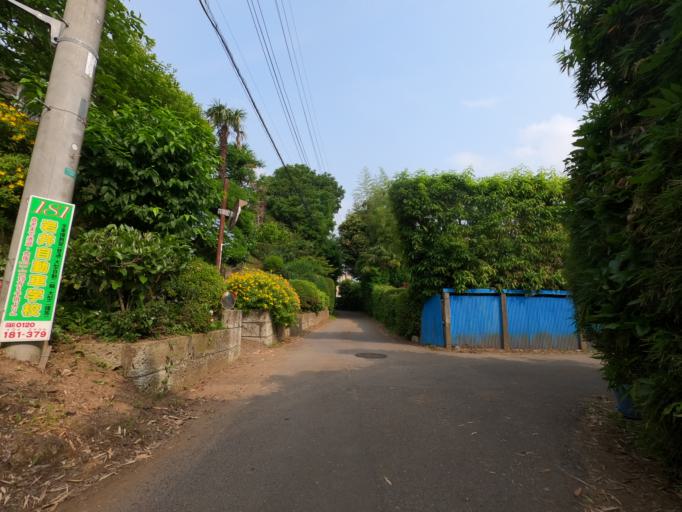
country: JP
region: Ibaraki
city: Moriya
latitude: 35.9604
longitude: 139.9517
